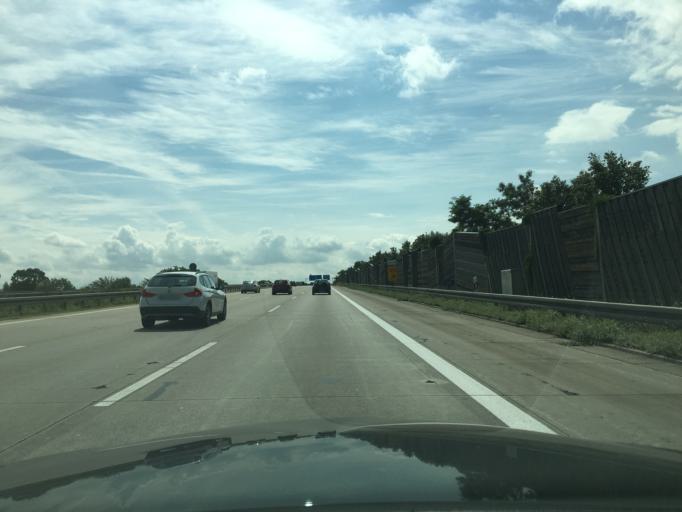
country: DE
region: Saxony-Anhalt
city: Gunthersdorf
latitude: 51.3567
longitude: 12.1883
